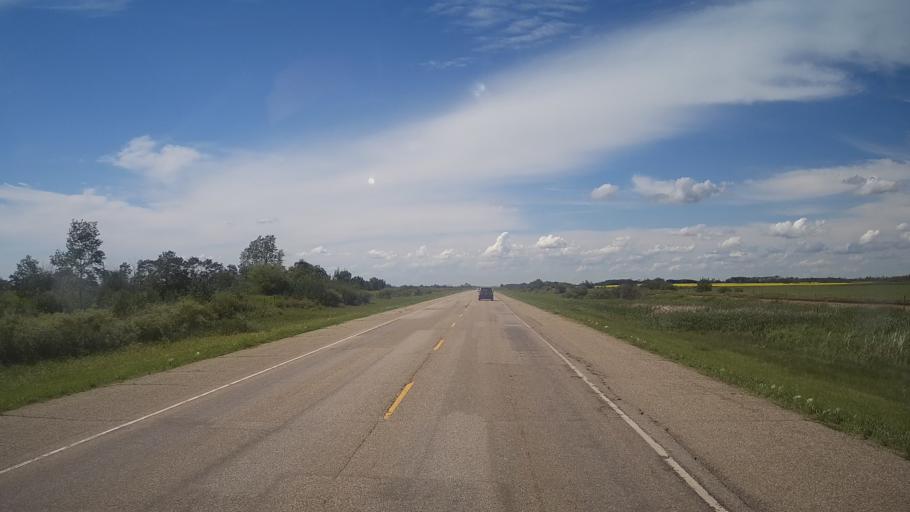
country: CA
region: Saskatchewan
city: Yorkton
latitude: 51.0704
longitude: -102.2252
